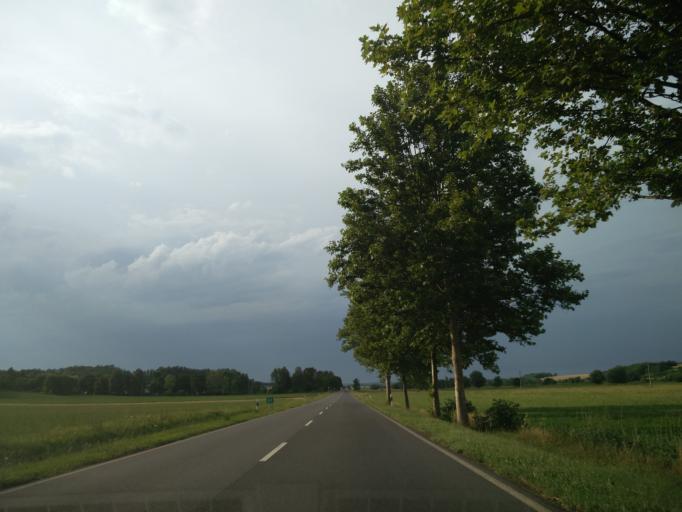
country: HU
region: Zala
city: Zalaegerszeg
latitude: 46.9490
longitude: 16.8482
